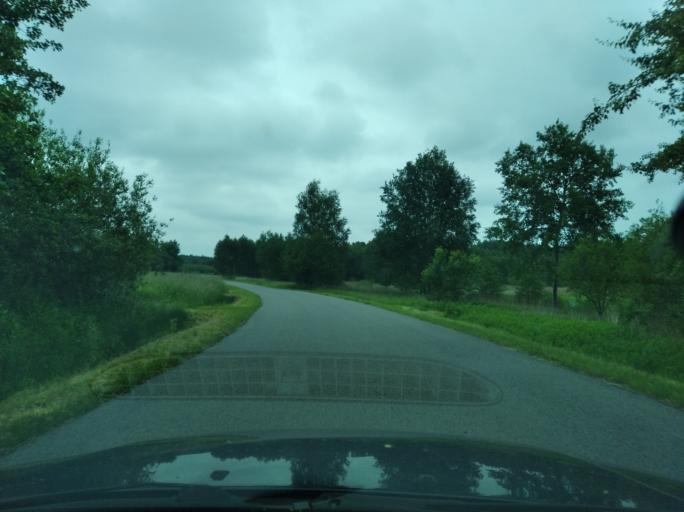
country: PL
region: Subcarpathian Voivodeship
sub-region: Powiat kolbuszowski
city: Niwiska
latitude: 50.2131
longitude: 21.6487
